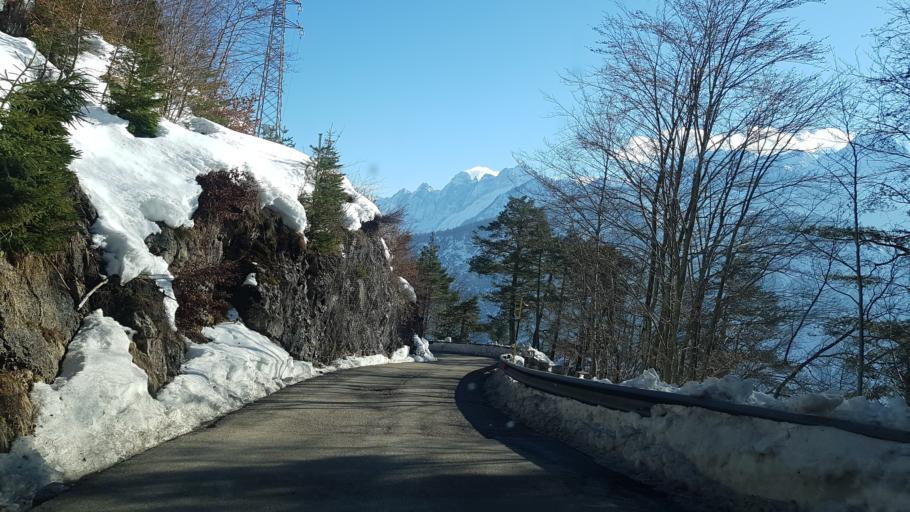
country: IT
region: Friuli Venezia Giulia
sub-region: Provincia di Udine
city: Malborghetto
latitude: 46.5185
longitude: 13.4707
